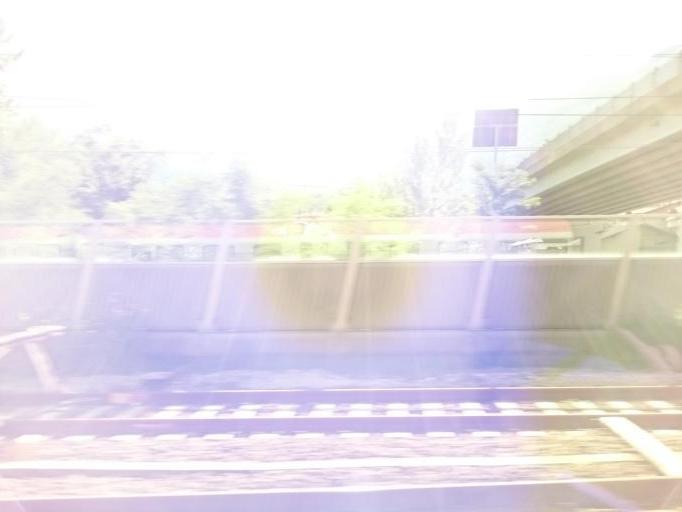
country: IT
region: Trentino-Alto Adige
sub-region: Provincia di Trento
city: Mattarello
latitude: 46.0093
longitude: 11.1259
